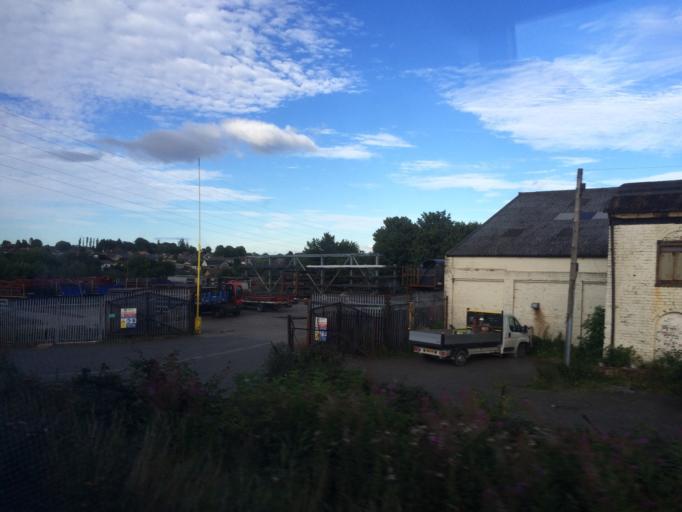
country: GB
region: Scotland
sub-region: Falkirk
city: Larbert
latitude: 56.0142
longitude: -3.8329
